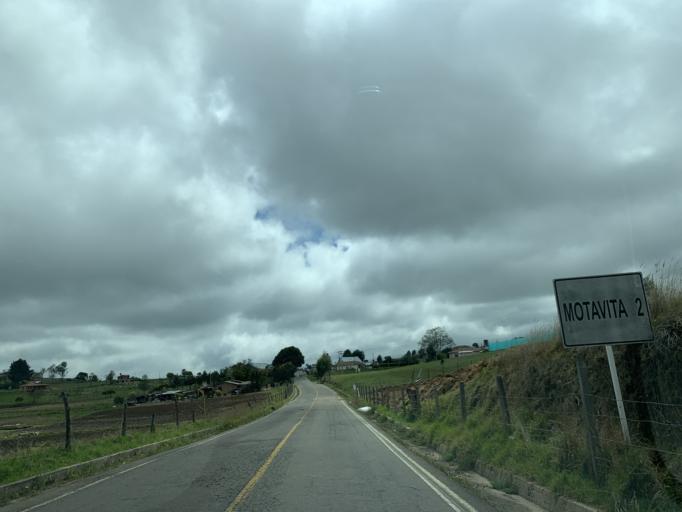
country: CO
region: Boyaca
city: Tunja
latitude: 5.5830
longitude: -73.3500
